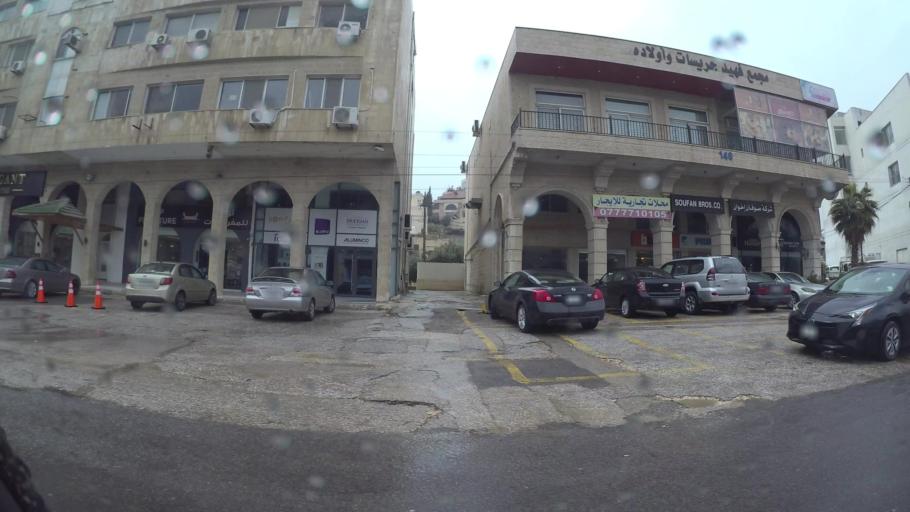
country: JO
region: Amman
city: Al Jubayhah
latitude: 32.0012
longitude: 35.8302
